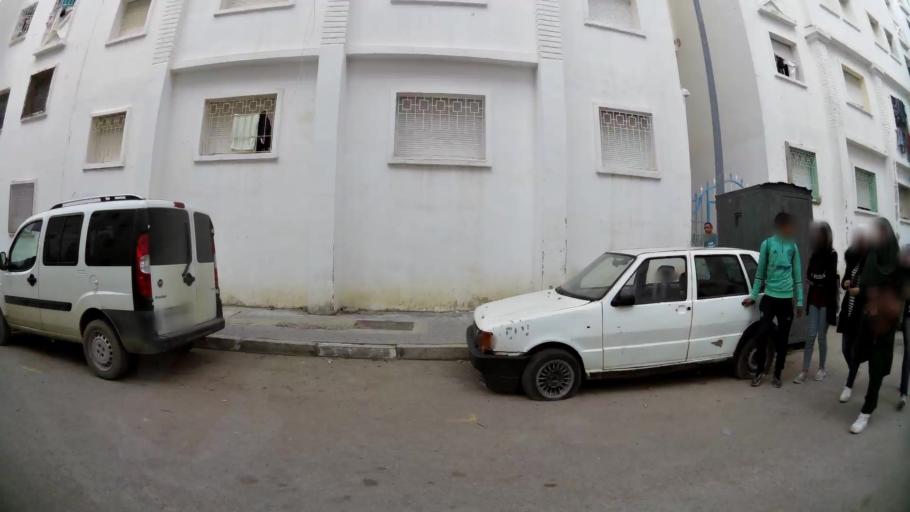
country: MA
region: Tanger-Tetouan
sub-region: Tanger-Assilah
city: Boukhalef
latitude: 35.7338
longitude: -5.8789
